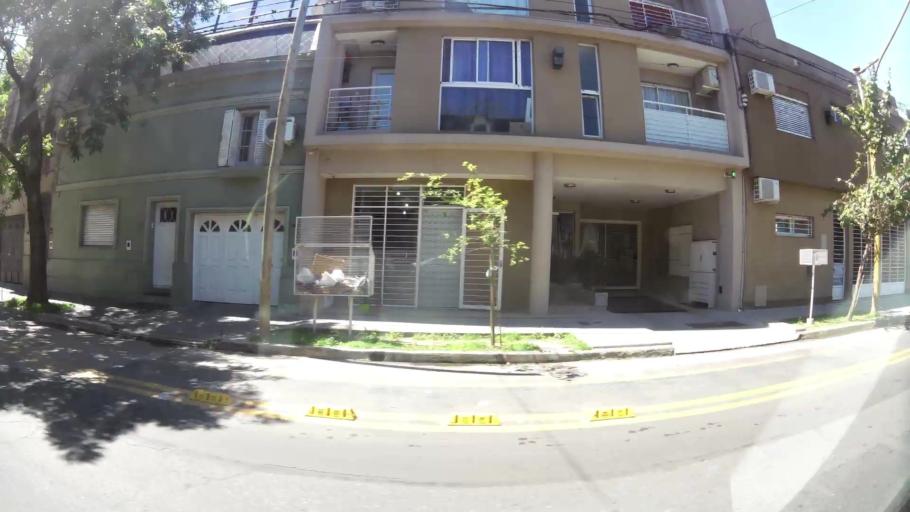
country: AR
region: Santa Fe
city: Santa Fe de la Vera Cruz
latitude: -31.6408
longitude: -60.6880
